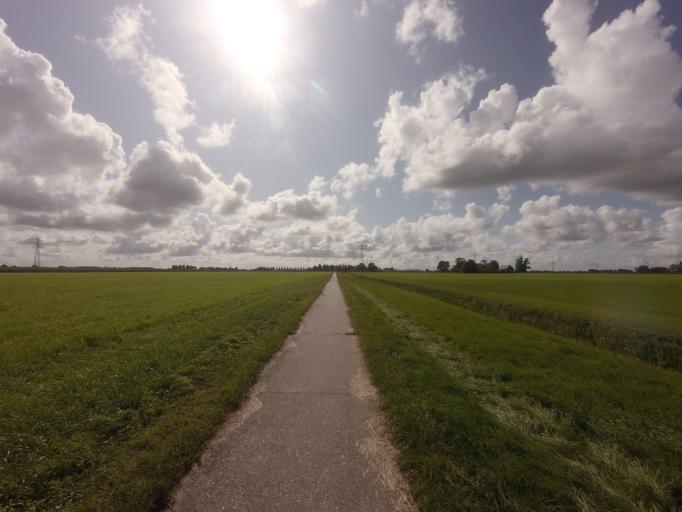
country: NL
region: Friesland
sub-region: Sudwest Fryslan
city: Sneek
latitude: 53.0653
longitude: 5.6368
